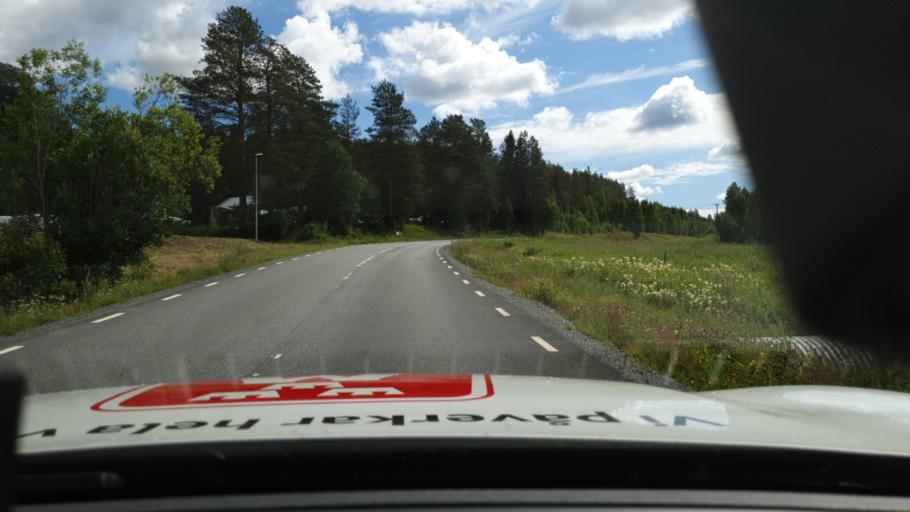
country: SE
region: Norrbotten
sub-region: Bodens Kommun
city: Saevast
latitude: 65.8304
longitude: 21.8814
